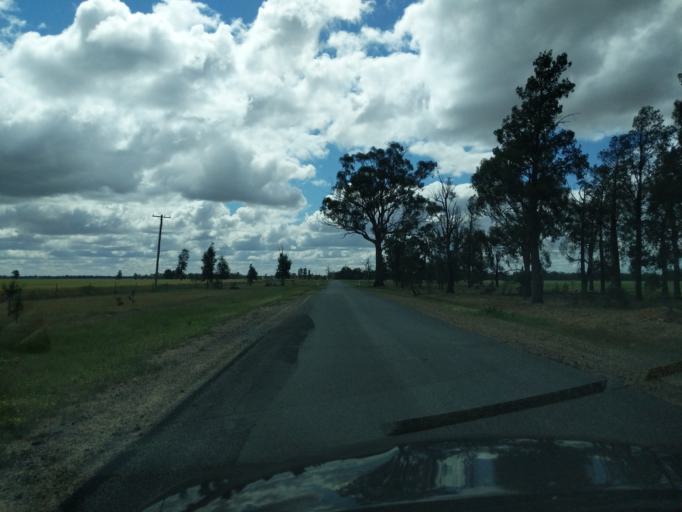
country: AU
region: New South Wales
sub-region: Coolamon
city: Coolamon
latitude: -34.8620
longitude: 146.8976
